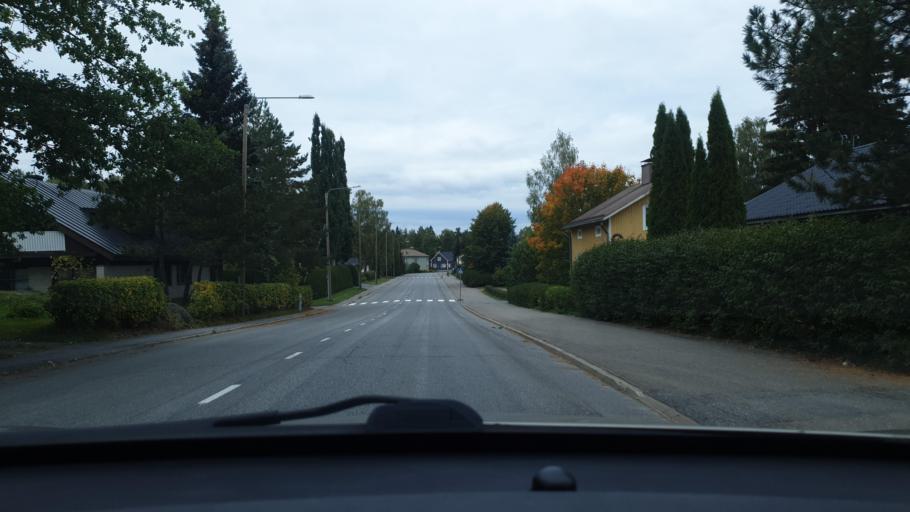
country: FI
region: Ostrobothnia
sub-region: Vaasa
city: Korsholm
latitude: 63.0916
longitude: 21.6653
